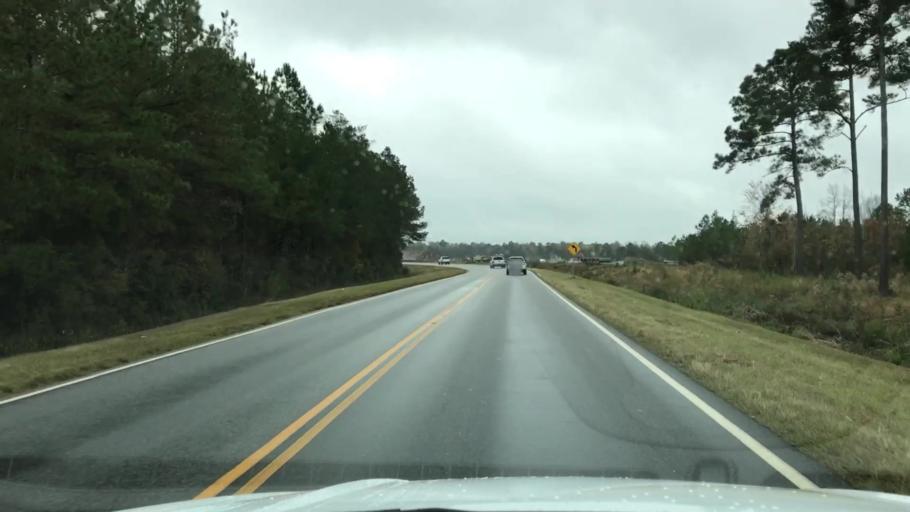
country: US
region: South Carolina
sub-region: Horry County
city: Myrtle Beach
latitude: 33.7571
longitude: -78.8835
